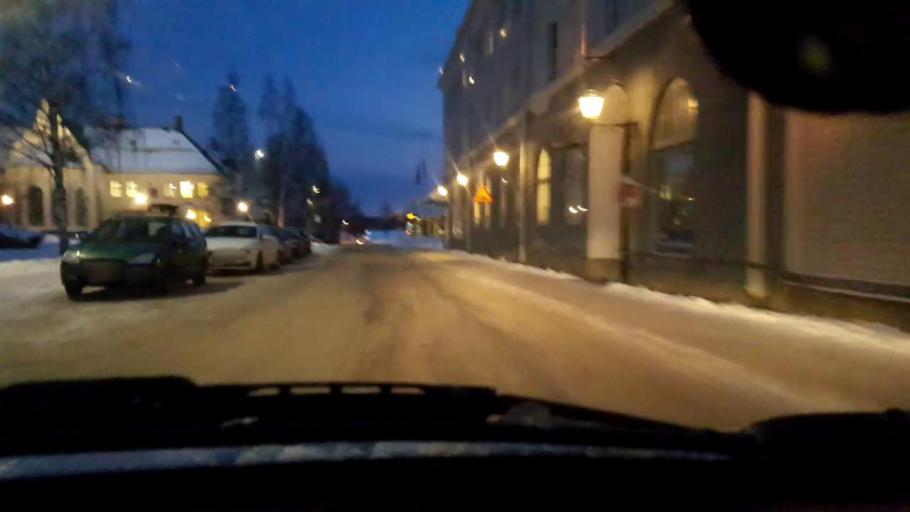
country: SE
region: Dalarna
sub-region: Mora Kommun
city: Mora
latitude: 61.0065
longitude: 14.5407
